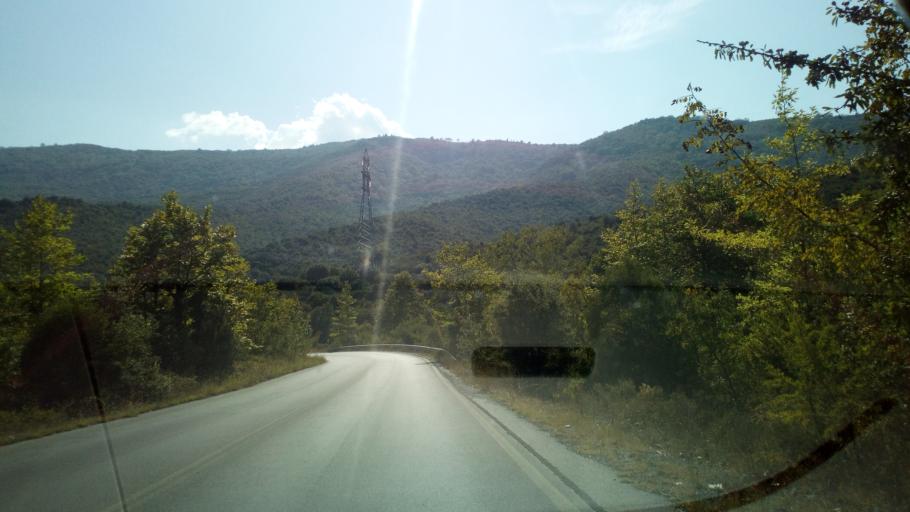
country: GR
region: Central Macedonia
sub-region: Nomos Thessalonikis
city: Stavros
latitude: 40.6488
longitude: 23.7453
